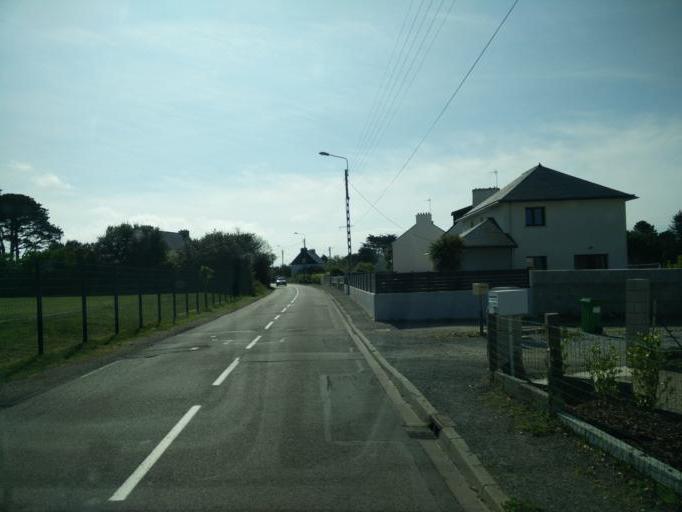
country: FR
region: Brittany
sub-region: Departement du Finistere
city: Crozon
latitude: 48.2439
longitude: -4.4817
